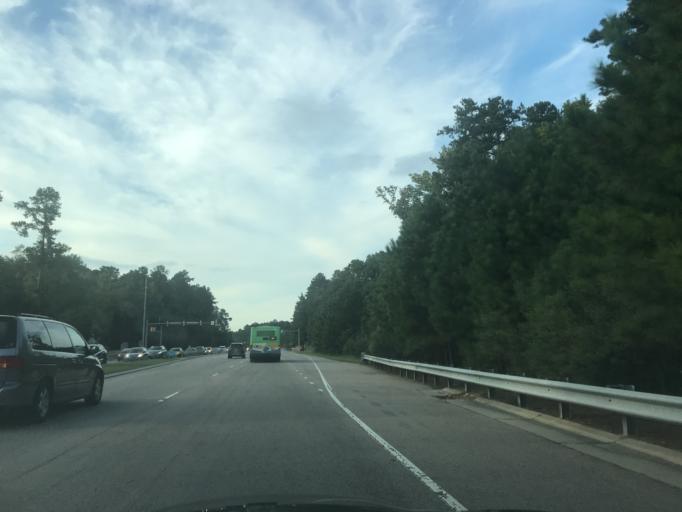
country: US
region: North Carolina
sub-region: Wake County
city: Green Level
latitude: 35.8188
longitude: -78.8734
